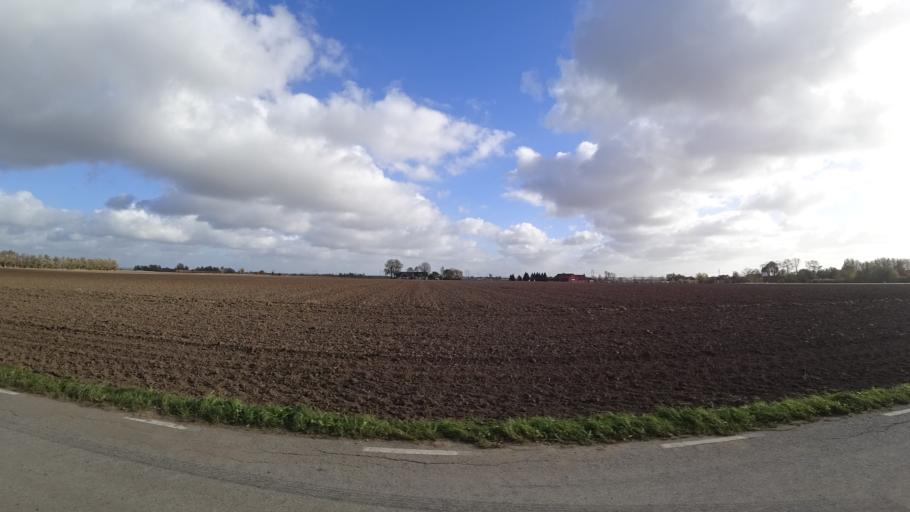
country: SE
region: Skane
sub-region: Staffanstorps Kommun
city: Hjaerup
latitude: 55.6443
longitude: 13.1508
